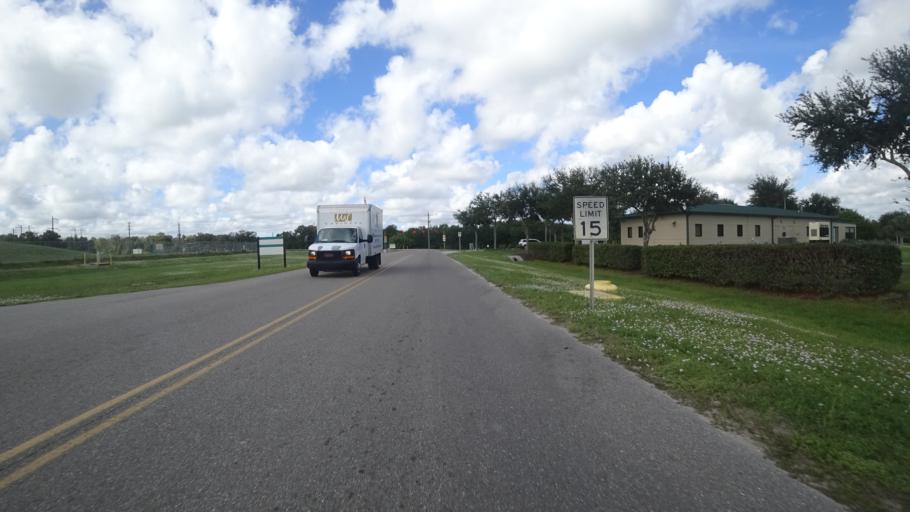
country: US
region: Florida
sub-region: Manatee County
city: Samoset
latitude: 27.4734
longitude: -82.4524
